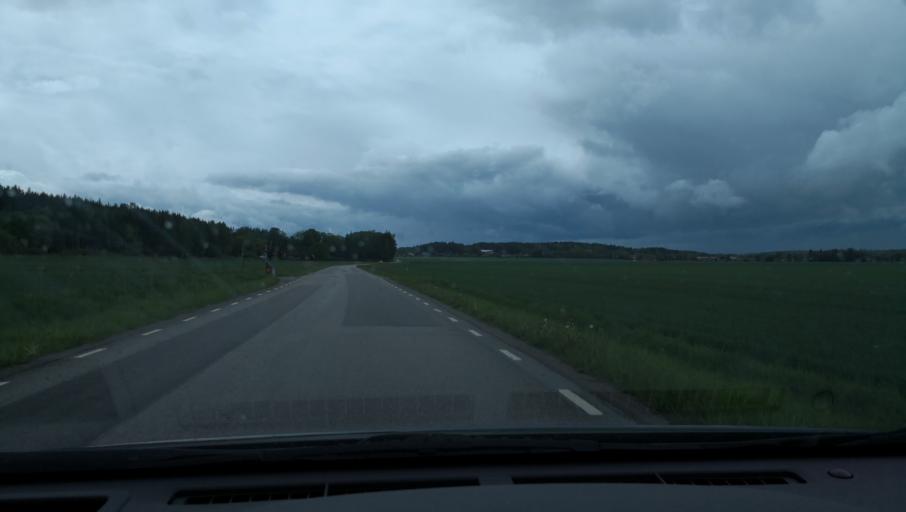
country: SE
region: Uppsala
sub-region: Enkopings Kommun
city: Orsundsbro
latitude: 59.7229
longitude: 17.3275
